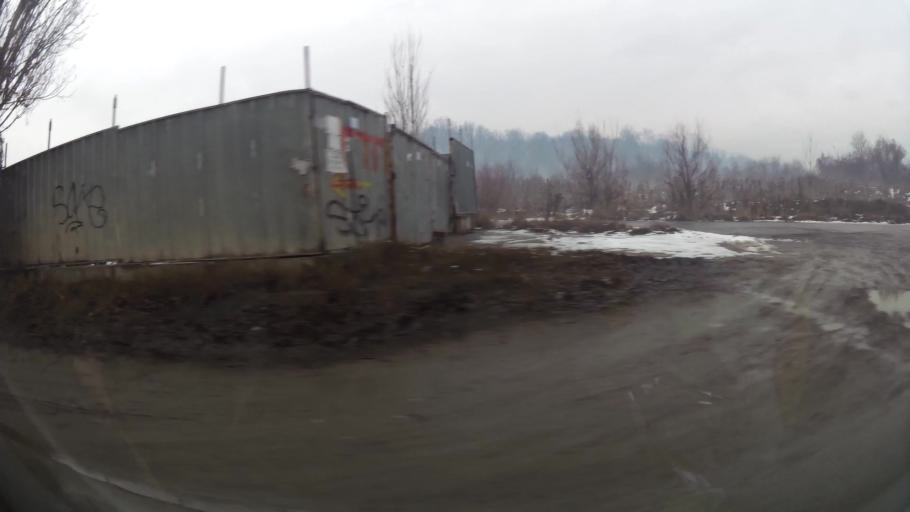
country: BG
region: Sofia-Capital
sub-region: Stolichna Obshtina
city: Sofia
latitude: 42.6877
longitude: 23.2688
